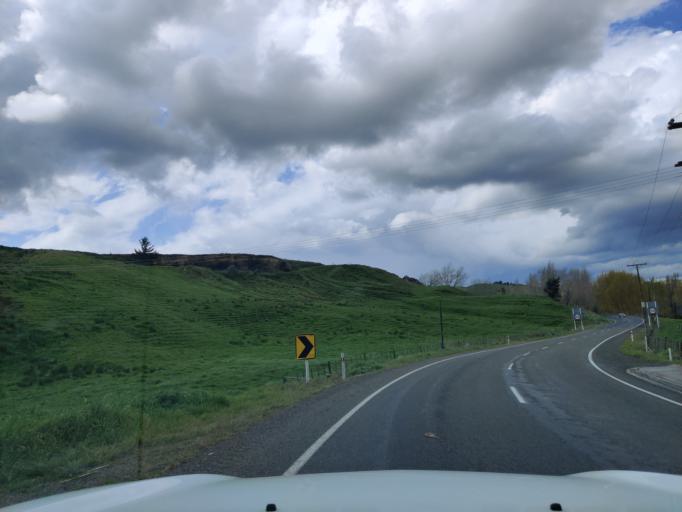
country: NZ
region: Manawatu-Wanganui
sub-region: Wanganui District
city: Wanganui
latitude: -39.8643
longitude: 175.1131
